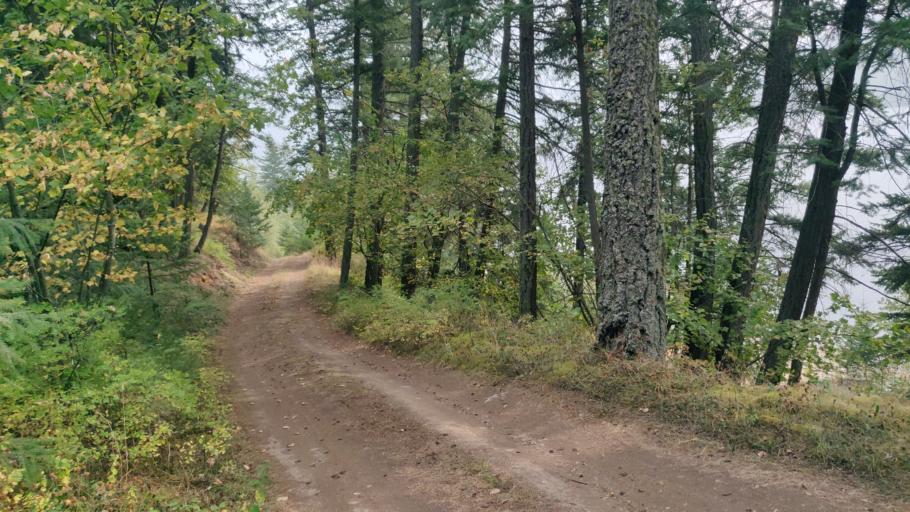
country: CA
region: British Columbia
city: Chase
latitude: 51.0764
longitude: -119.7647
